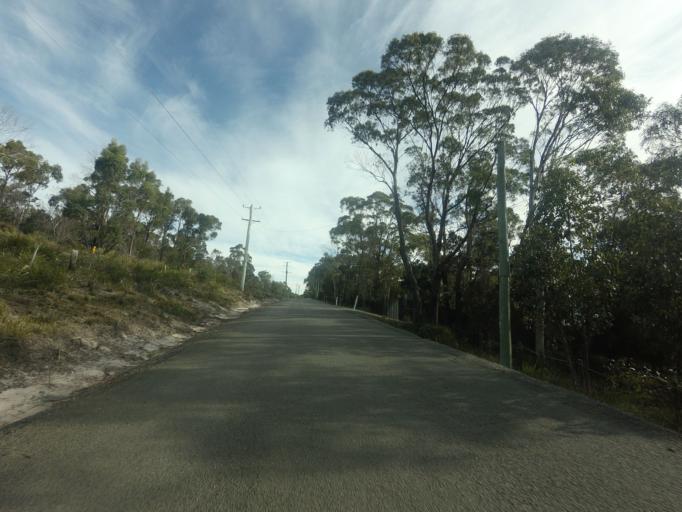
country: AU
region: Tasmania
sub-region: Sorell
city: Sorell
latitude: -42.9590
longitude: 147.8409
